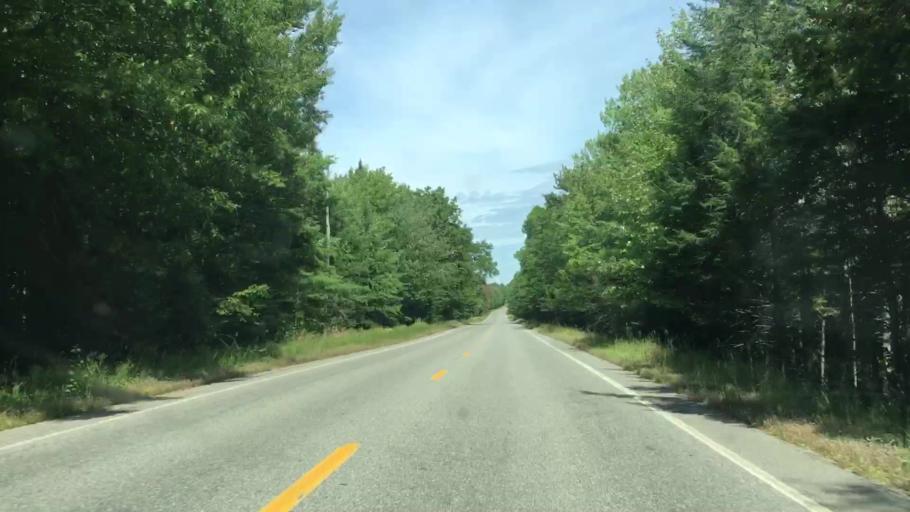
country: US
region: Maine
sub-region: Penobscot County
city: Lincoln
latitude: 45.3836
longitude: -68.5424
